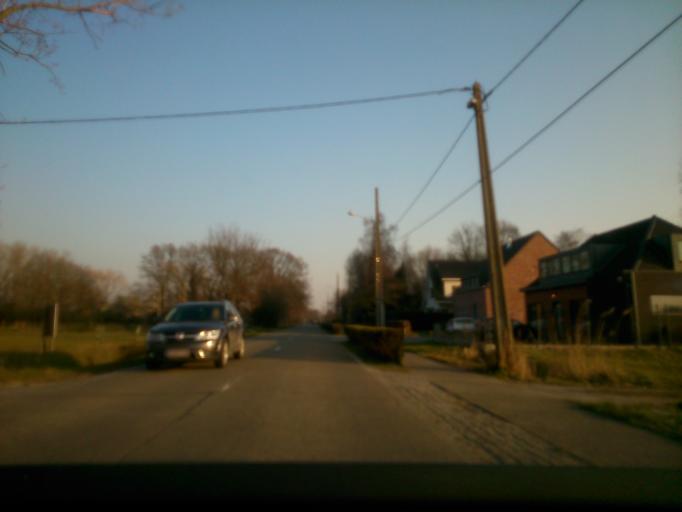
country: BE
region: Flanders
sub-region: Provincie Antwerpen
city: Stabroek
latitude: 51.3402
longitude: 4.3512
